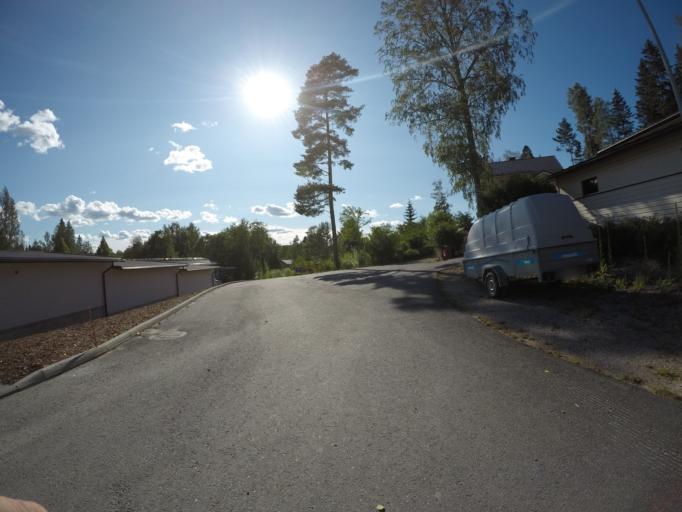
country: FI
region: Haeme
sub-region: Haemeenlinna
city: Haemeenlinna
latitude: 61.0187
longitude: 24.5051
